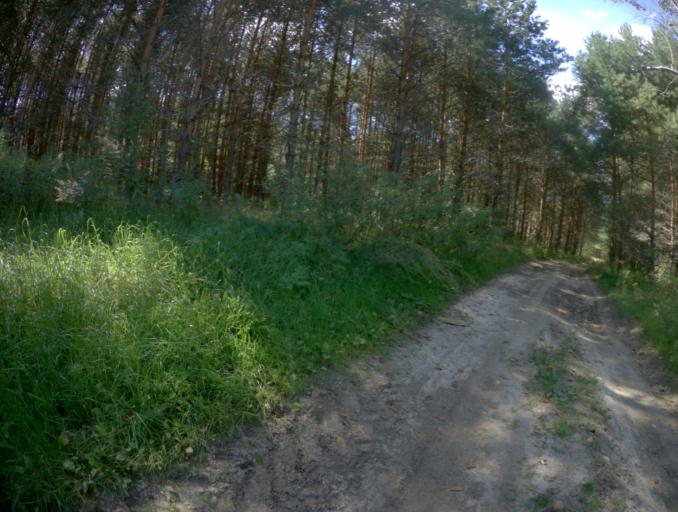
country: RU
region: Vladimir
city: Krasnaya Gorbatka
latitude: 55.9969
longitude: 41.8872
